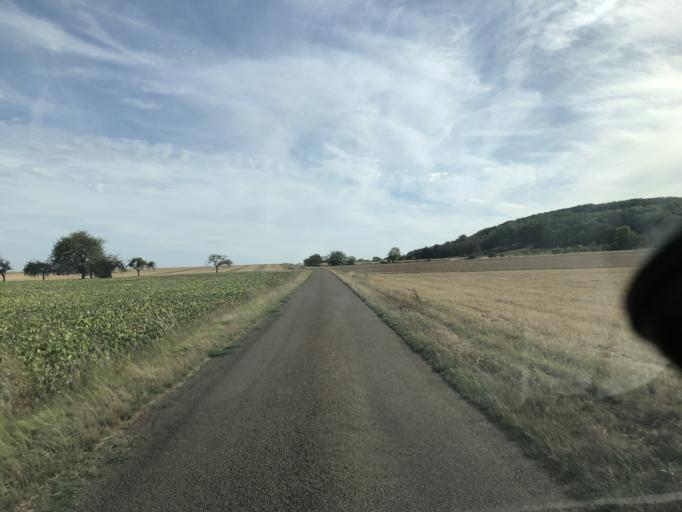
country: FR
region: Bourgogne
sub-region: Departement de l'Yonne
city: Joigny
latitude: 47.9472
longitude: 3.3939
